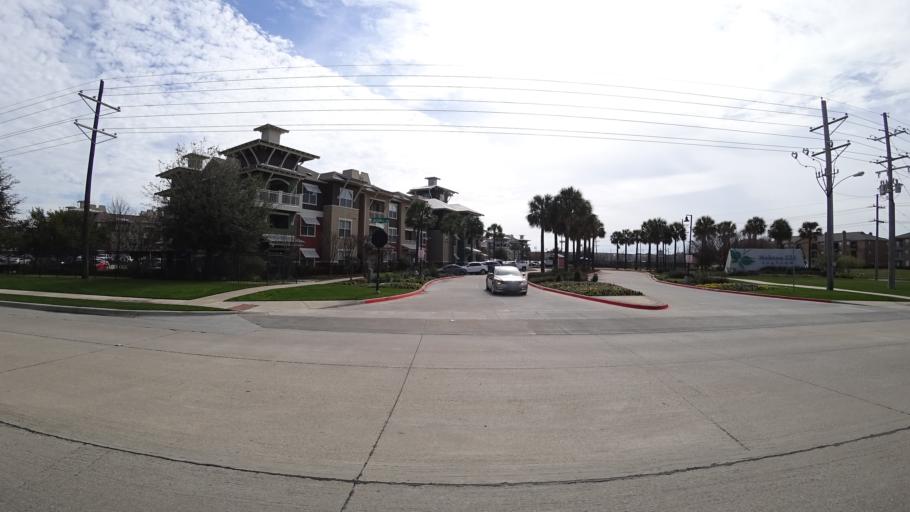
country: US
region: Texas
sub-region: Denton County
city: Lewisville
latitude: 33.0084
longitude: -96.9627
